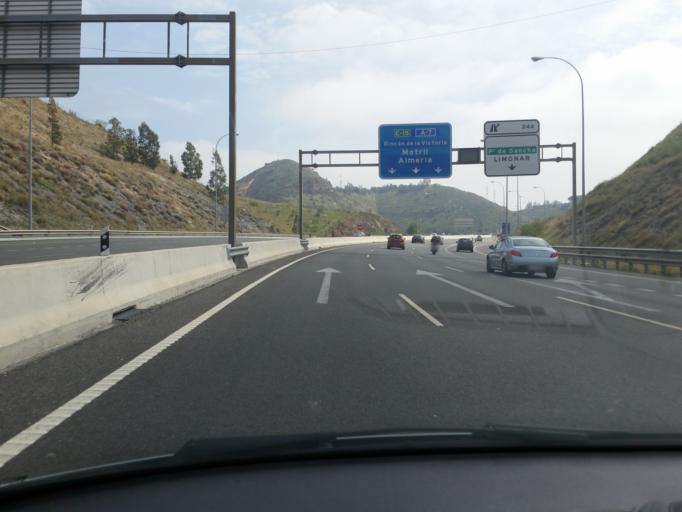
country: ES
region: Andalusia
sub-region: Provincia de Malaga
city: Malaga
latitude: 36.7397
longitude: -4.3979
